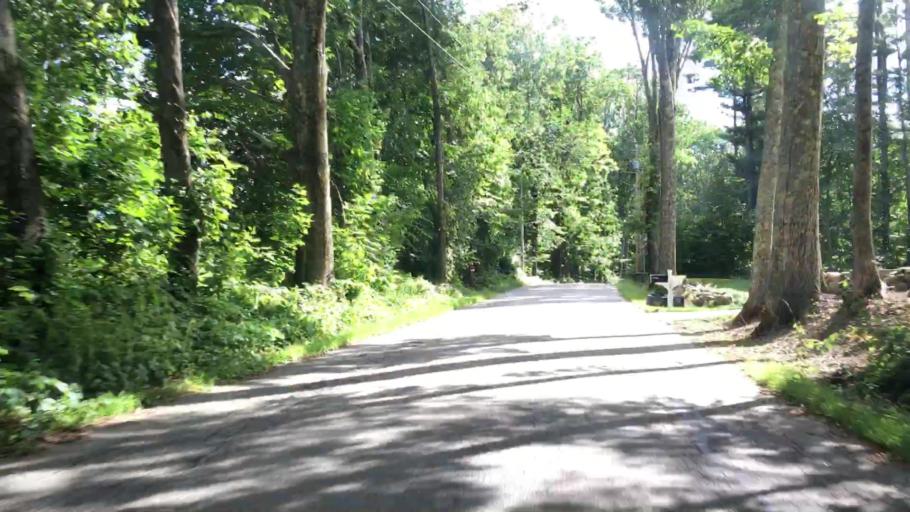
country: US
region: New Hampshire
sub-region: Strafford County
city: Madbury
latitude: 43.1641
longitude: -70.9168
